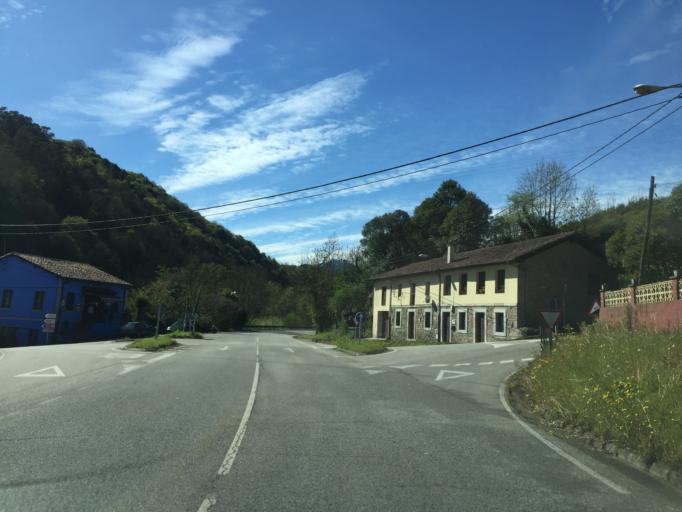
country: ES
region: Asturias
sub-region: Province of Asturias
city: Proaza
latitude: 43.3381
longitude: -5.9857
